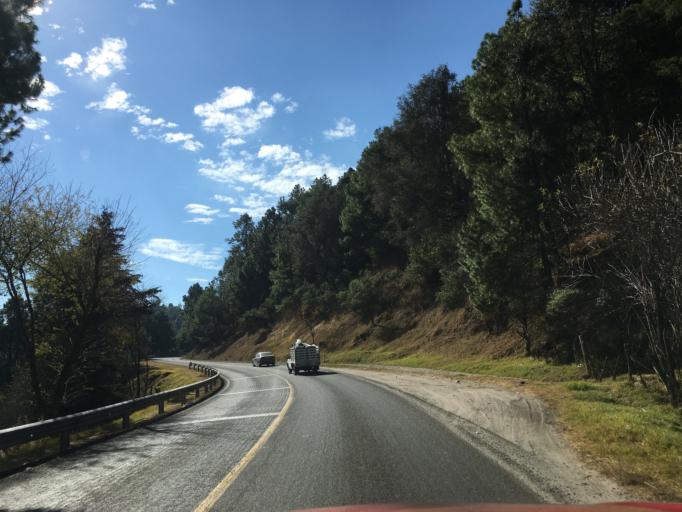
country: MX
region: Michoacan
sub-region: Hidalgo
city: Tierras Coloradas (San Pedro)
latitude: 19.7118
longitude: -100.7496
